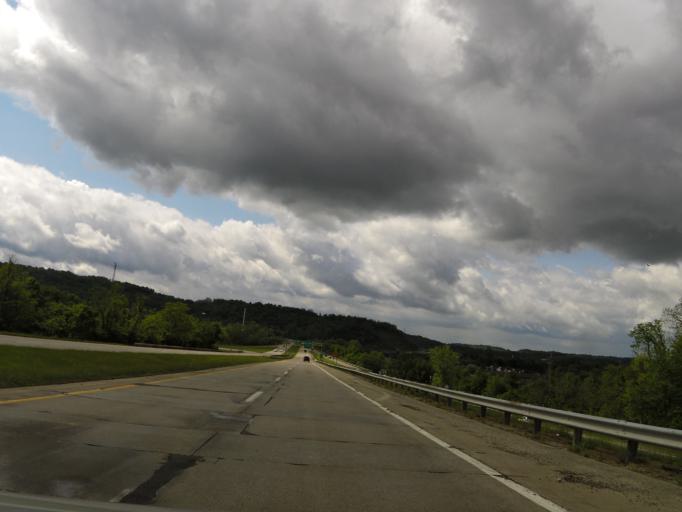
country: US
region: Ohio
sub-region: Athens County
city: Athens
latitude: 39.3397
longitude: -82.0814
